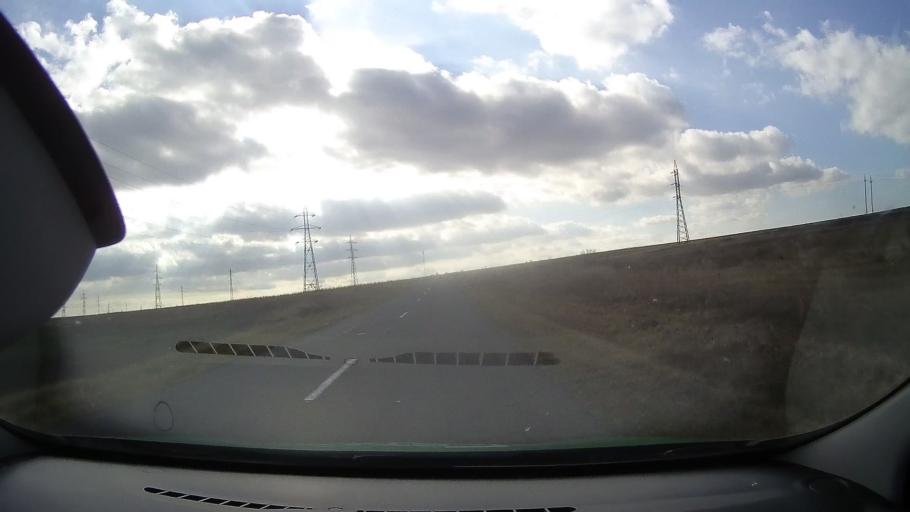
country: RO
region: Constanta
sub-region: Comuna Sacele
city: Sacele
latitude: 44.4962
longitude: 28.6576
